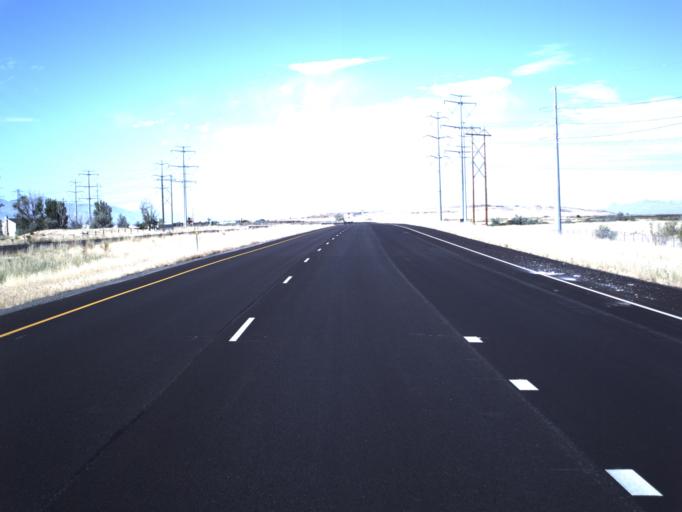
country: US
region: Utah
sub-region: Davis County
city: West Bountiful
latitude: 40.9170
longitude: -111.9041
